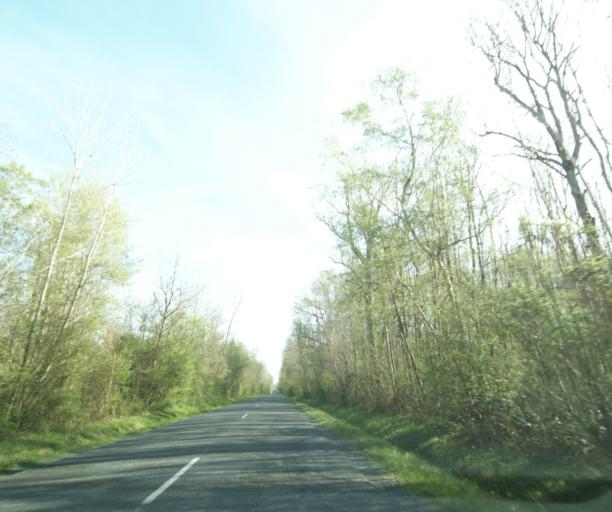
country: FR
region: Ile-de-France
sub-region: Departement de Seine-et-Marne
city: Nangis
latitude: 48.5253
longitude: 2.9749
